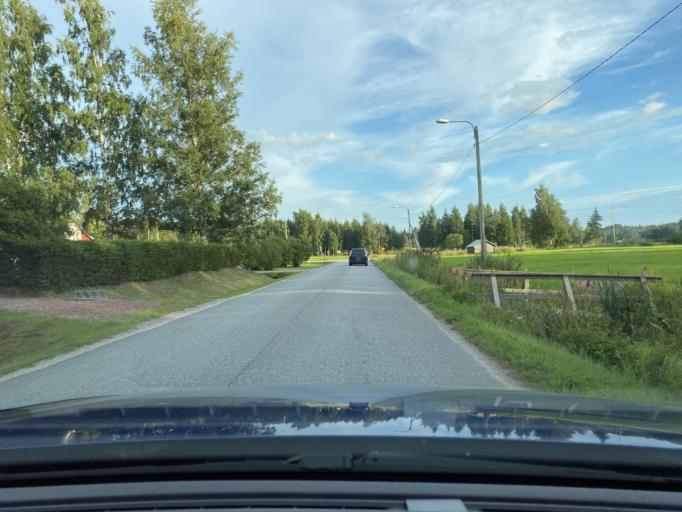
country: FI
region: Ostrobothnia
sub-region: Vaasa
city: Korsnaes
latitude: 62.9660
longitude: 21.1913
